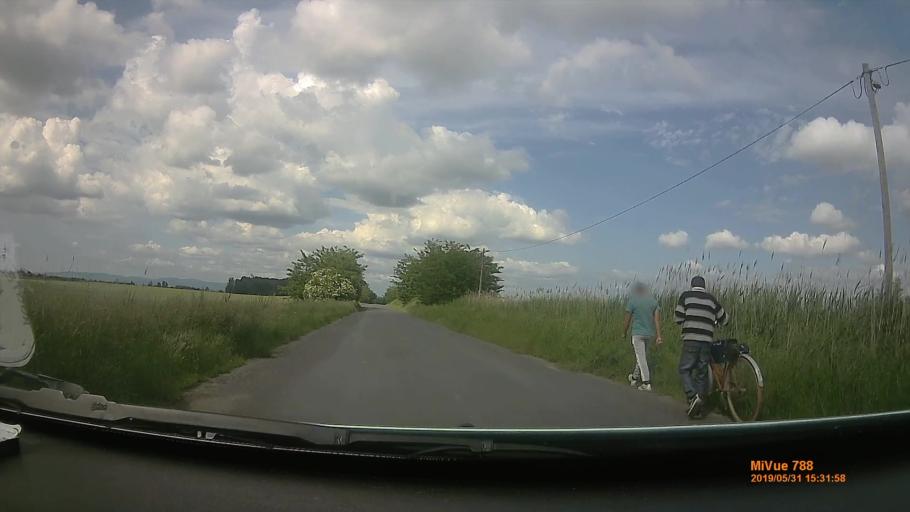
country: HU
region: Borsod-Abauj-Zemplen
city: Prugy
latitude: 48.0675
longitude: 21.2358
